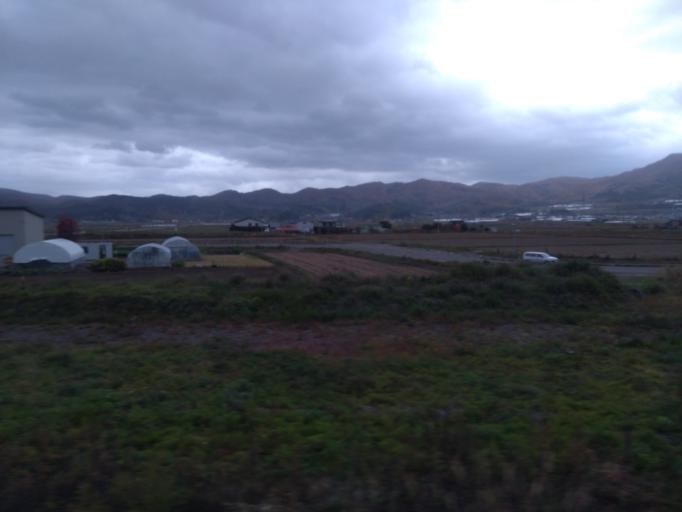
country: JP
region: Hokkaido
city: Nanae
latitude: 41.9032
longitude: 140.6559
